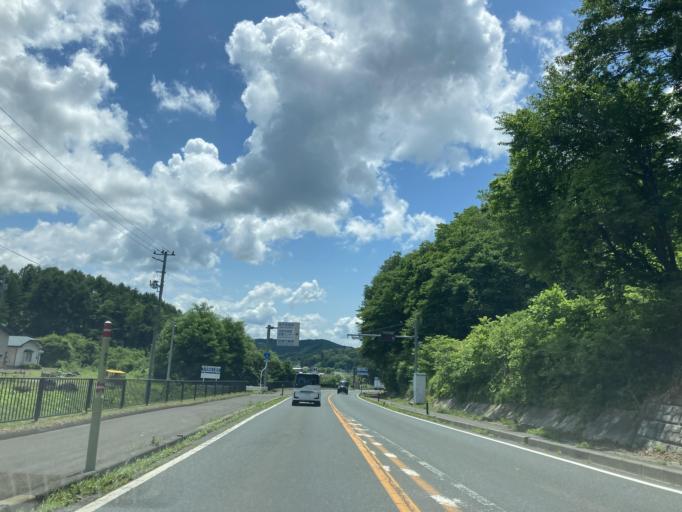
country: JP
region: Iwate
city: Ichinohe
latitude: 39.9717
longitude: 141.2142
